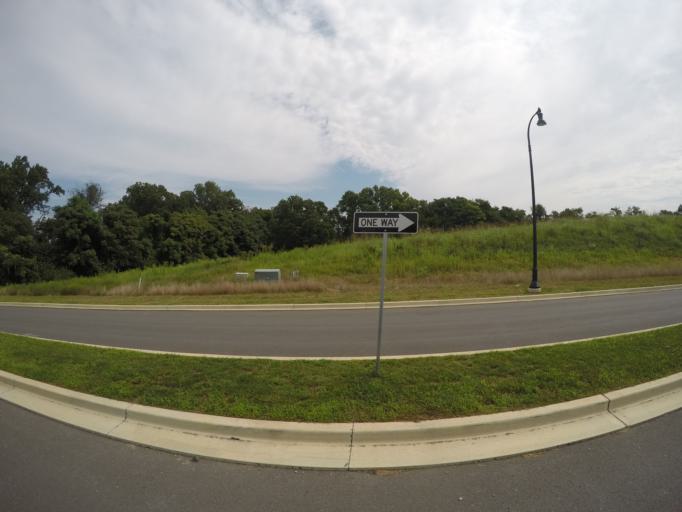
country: US
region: Maryland
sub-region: Montgomery County
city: Clarksburg
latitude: 39.2220
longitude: -77.2855
